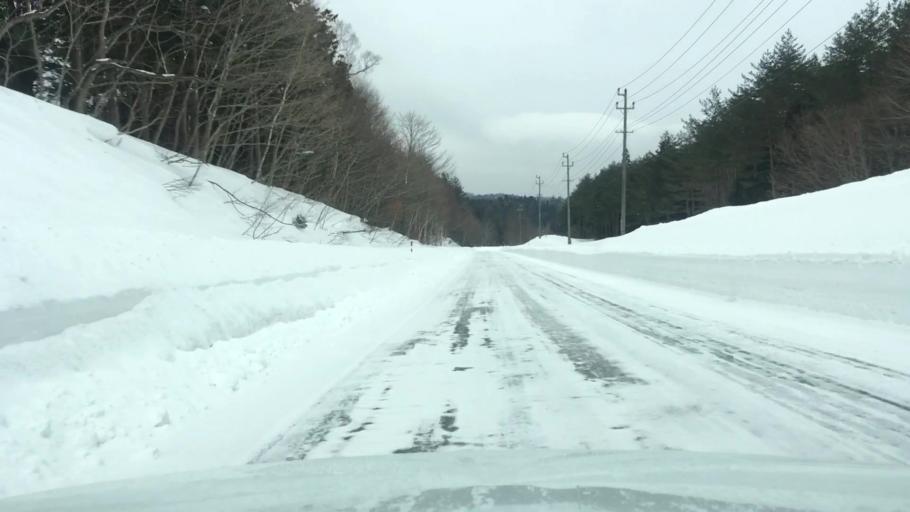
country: JP
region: Akita
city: Hanawa
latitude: 39.9871
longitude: 141.0000
